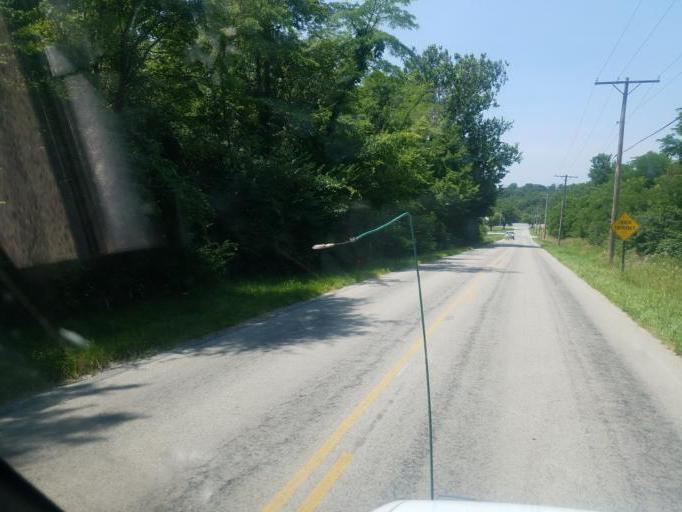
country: US
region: Ohio
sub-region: Shelby County
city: Sidney
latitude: 40.3032
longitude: -84.1346
